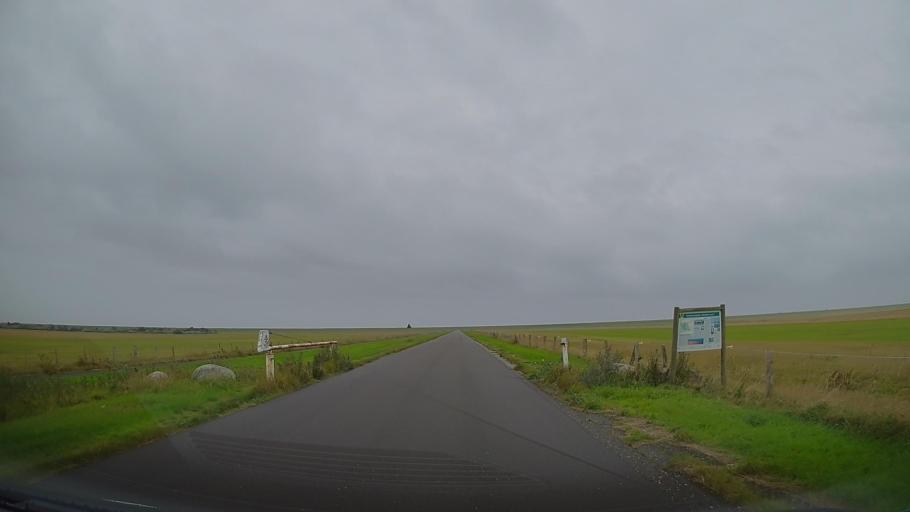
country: DE
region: Schleswig-Holstein
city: Friedrichsgabekoog
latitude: 54.1164
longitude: 8.9509
